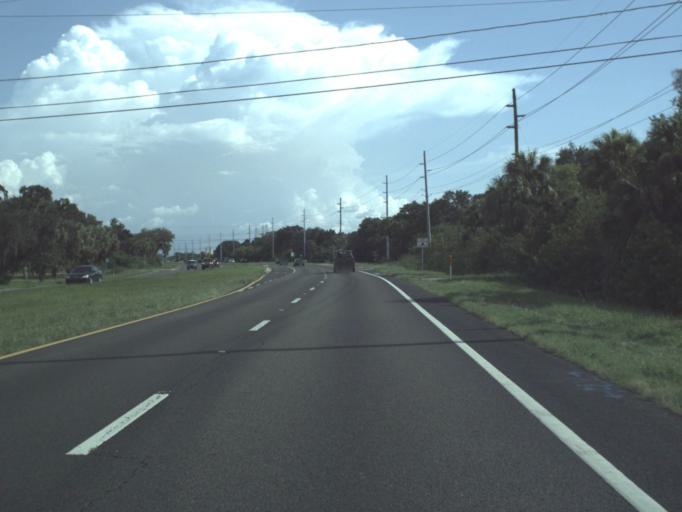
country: US
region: Florida
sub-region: Hillsborough County
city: Gibsonton
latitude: 27.8164
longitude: -82.3837
